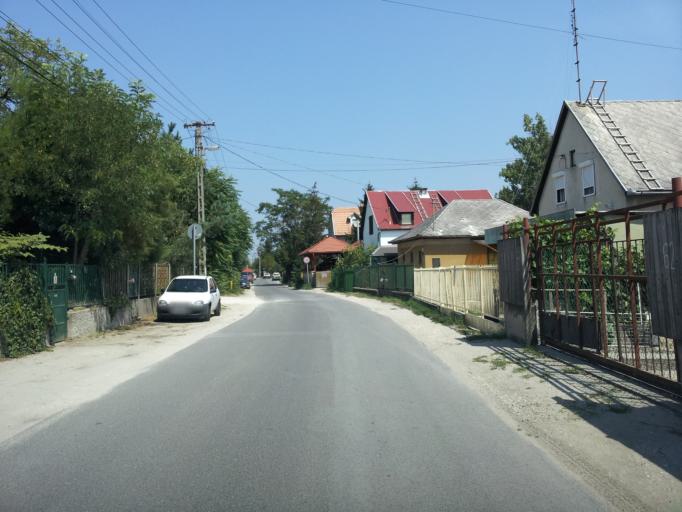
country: HU
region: Pest
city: Szigetszentmiklos
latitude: 47.3274
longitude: 19.0443
